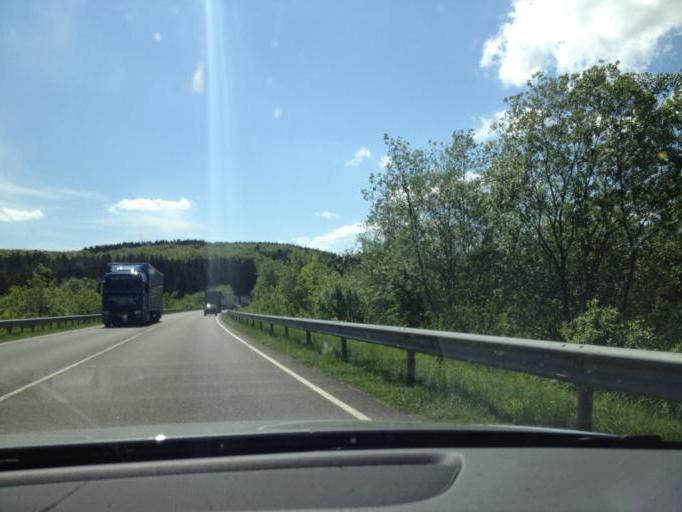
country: DE
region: Rheinland-Pfalz
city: Oberlauch
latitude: 50.1776
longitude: 6.4124
